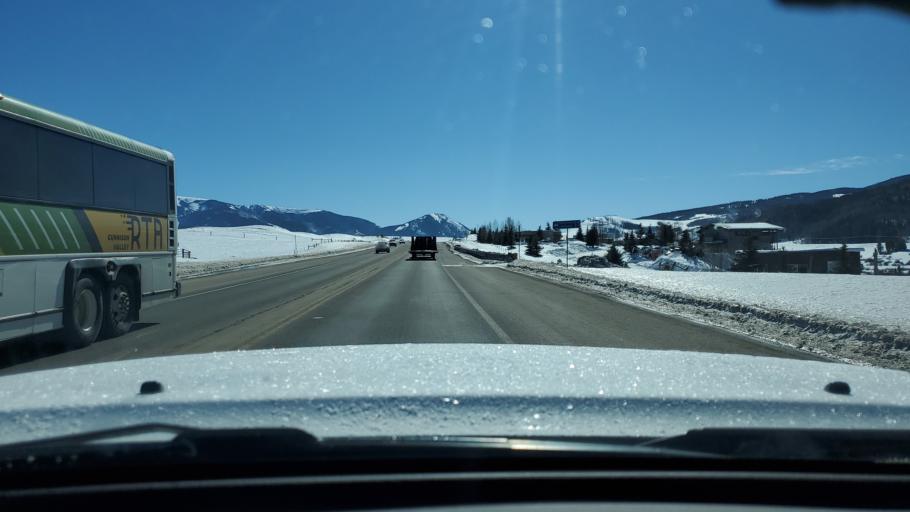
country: US
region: Colorado
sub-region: Gunnison County
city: Crested Butte
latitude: 38.8510
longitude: -106.9524
